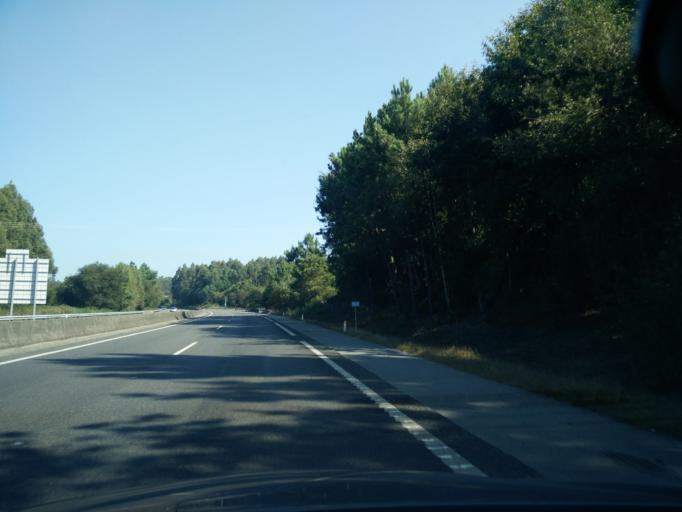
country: ES
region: Galicia
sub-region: Provincia da Coruna
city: Mino
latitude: 43.3807
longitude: -8.1802
